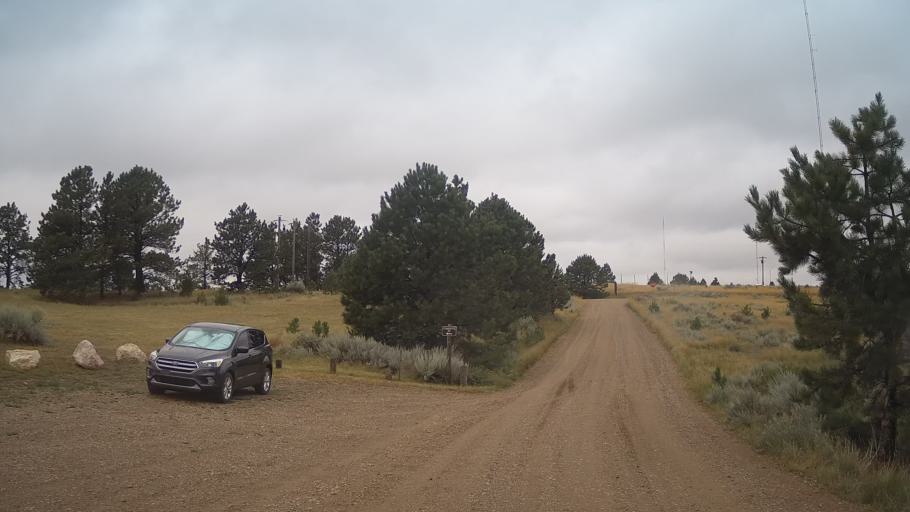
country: US
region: Montana
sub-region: Dawson County
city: Glendive
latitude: 47.0513
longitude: -104.6764
